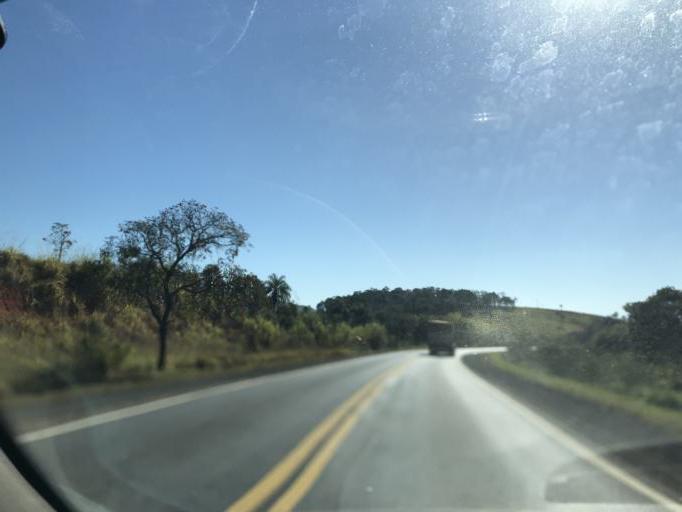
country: BR
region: Minas Gerais
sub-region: Bambui
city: Bambui
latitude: -19.8539
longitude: -45.9935
